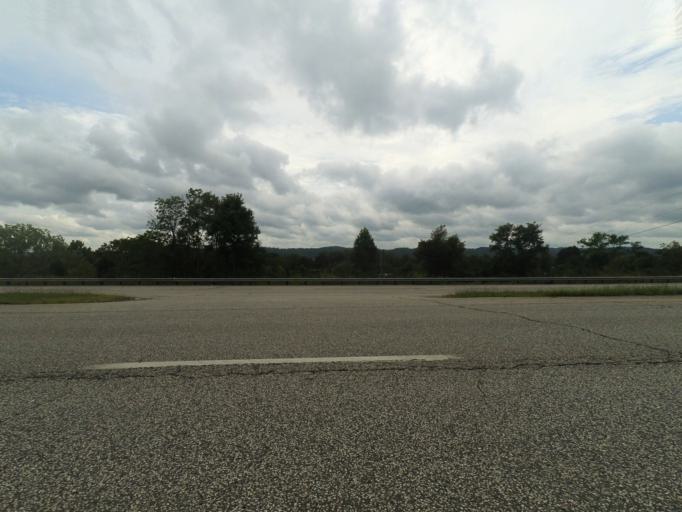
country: US
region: West Virginia
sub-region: Cabell County
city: Huntington
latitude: 38.4271
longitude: -82.4732
